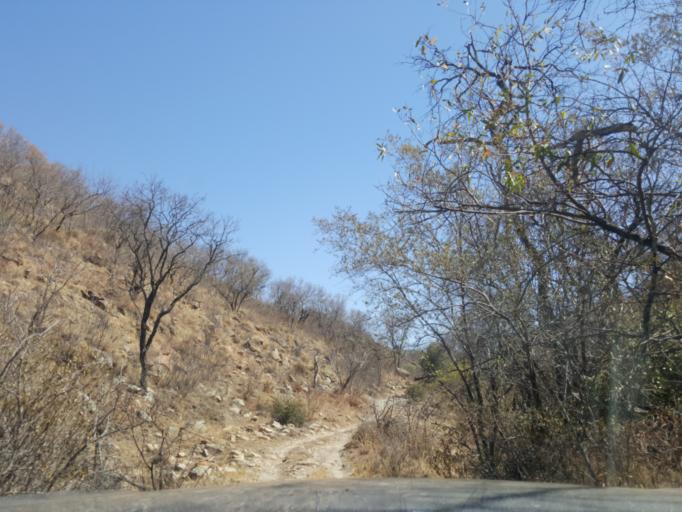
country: BW
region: South East
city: Lobatse
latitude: -25.1526
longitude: 25.6718
